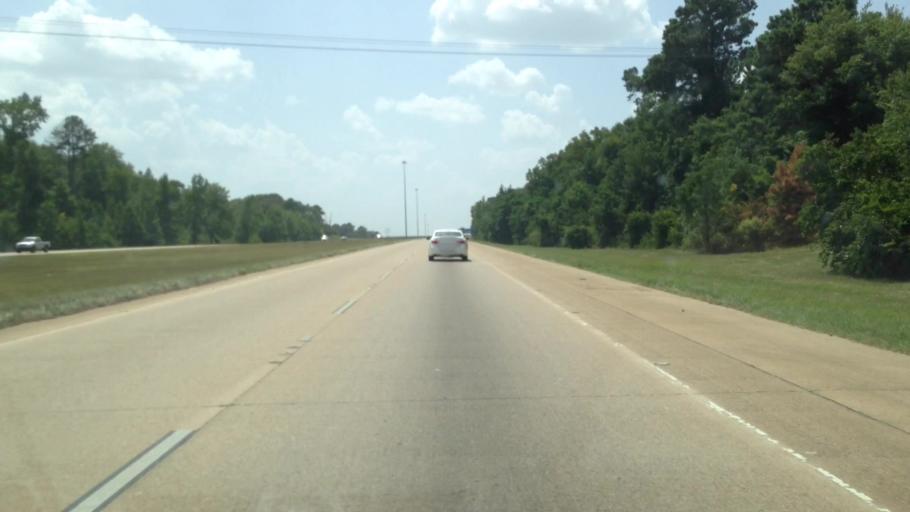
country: US
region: Louisiana
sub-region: Lincoln Parish
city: Grambling
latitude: 32.5408
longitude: -92.7038
